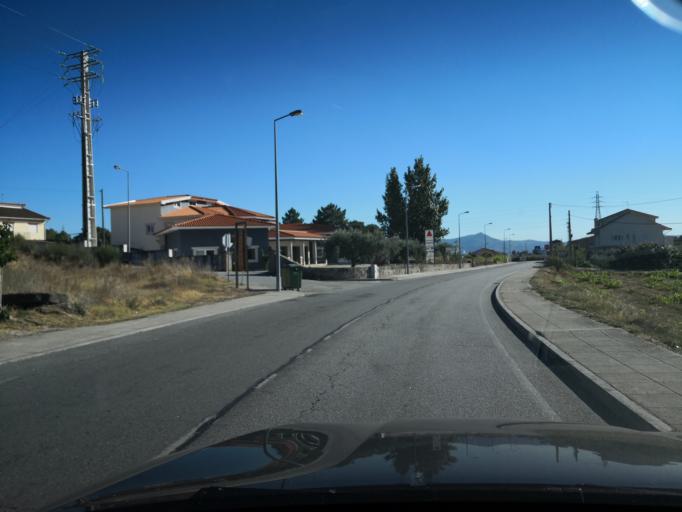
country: PT
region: Vila Real
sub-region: Valpacos
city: Valpacos
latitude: 41.6232
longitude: -7.3120
